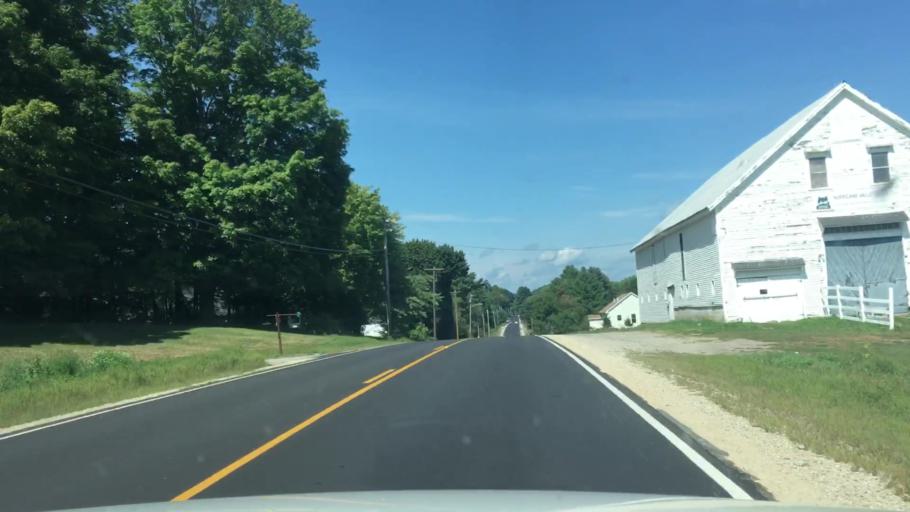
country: US
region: Maine
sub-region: Cumberland County
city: Cumberland Center
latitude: 43.7869
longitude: -70.3046
